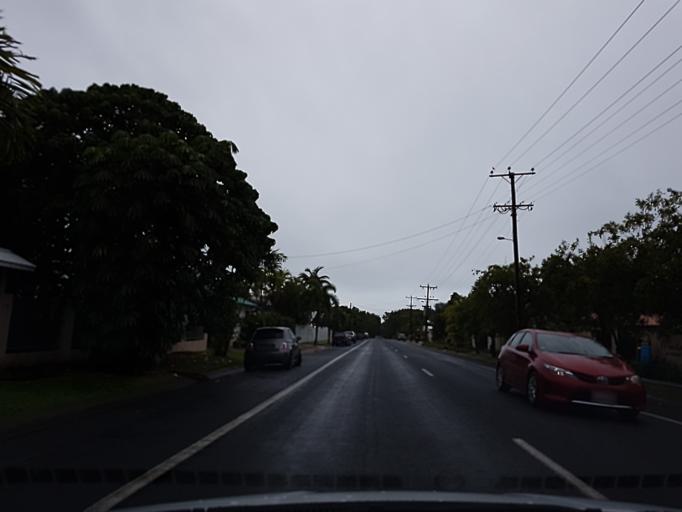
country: AU
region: Queensland
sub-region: Cairns
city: Palm Cove
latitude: -16.7456
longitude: 145.6656
